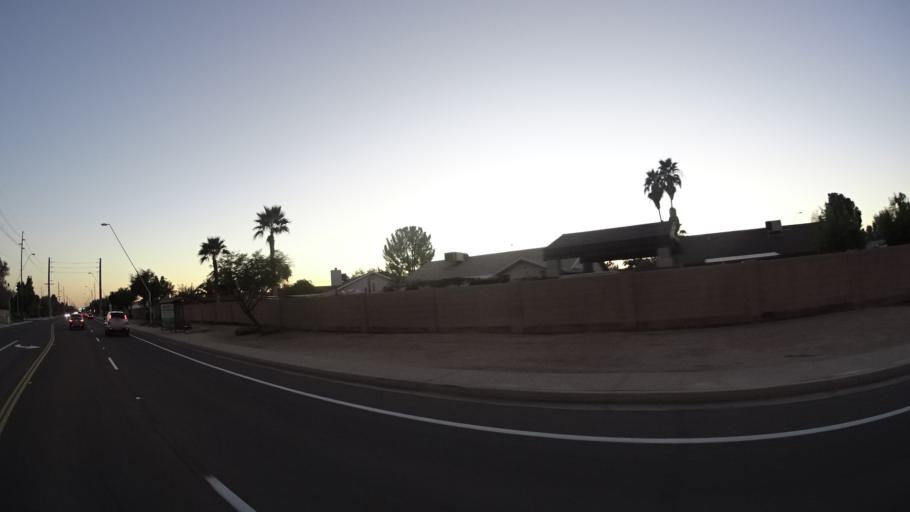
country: US
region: Arizona
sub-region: Maricopa County
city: San Carlos
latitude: 33.3310
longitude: -111.8765
